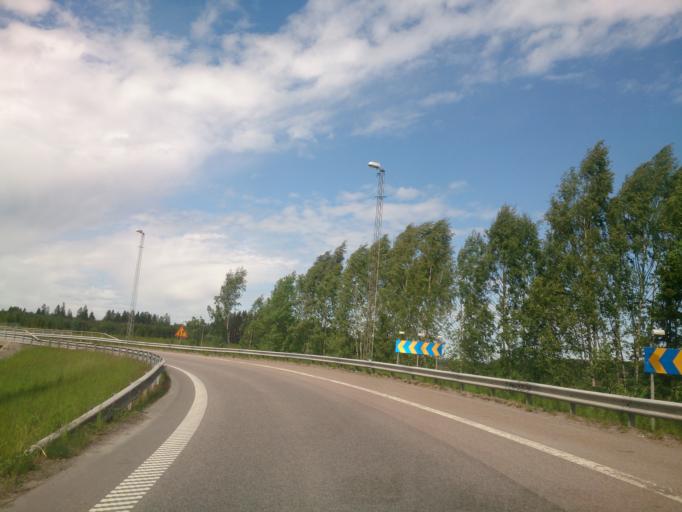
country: SE
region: OEstergoetland
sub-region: Linkopings Kommun
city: Malmslatt
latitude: 58.4116
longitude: 15.5490
